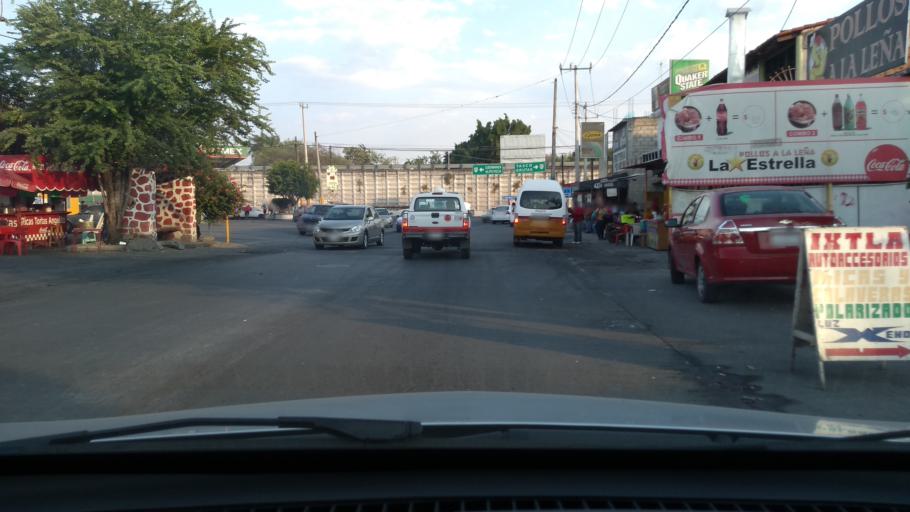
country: MX
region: Morelos
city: Puente de Ixtla
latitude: 18.6326
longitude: -99.3232
